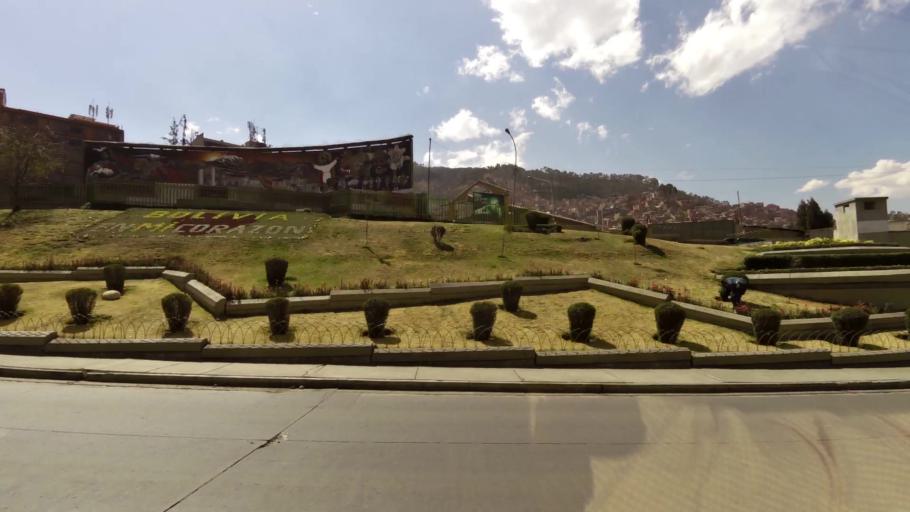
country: BO
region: La Paz
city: La Paz
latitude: -16.4894
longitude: -68.1431
